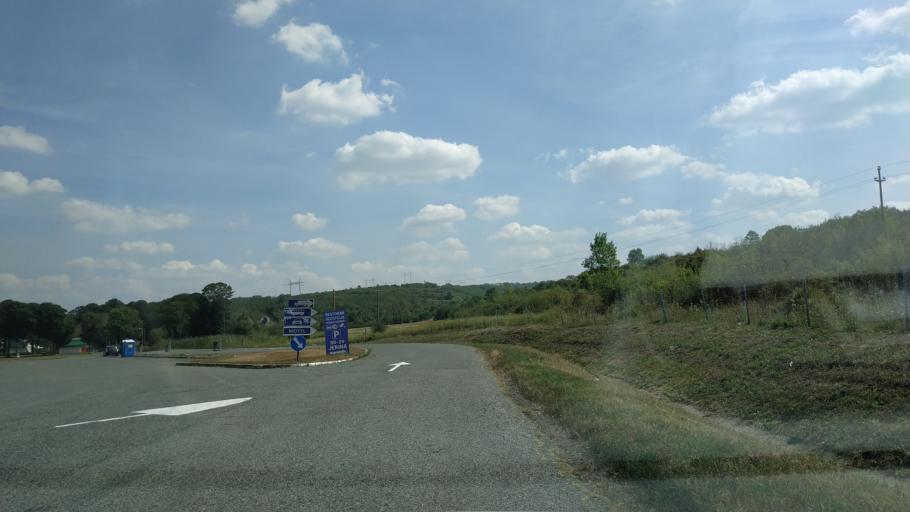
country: RS
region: Central Serbia
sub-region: Belgrade
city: Grocka
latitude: 44.5829
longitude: 20.8132
